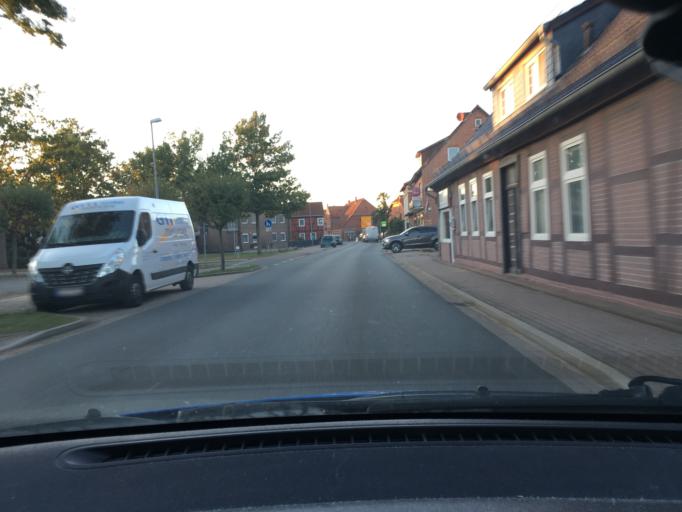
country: DE
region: Lower Saxony
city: Bleckede
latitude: 53.2902
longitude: 10.7349
